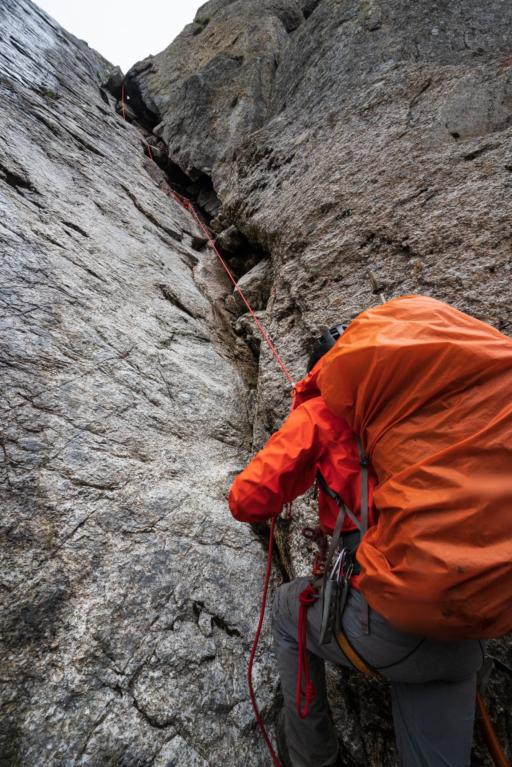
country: RU
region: Transbaikal Territory
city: Chara
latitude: 56.8660
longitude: 117.3803
